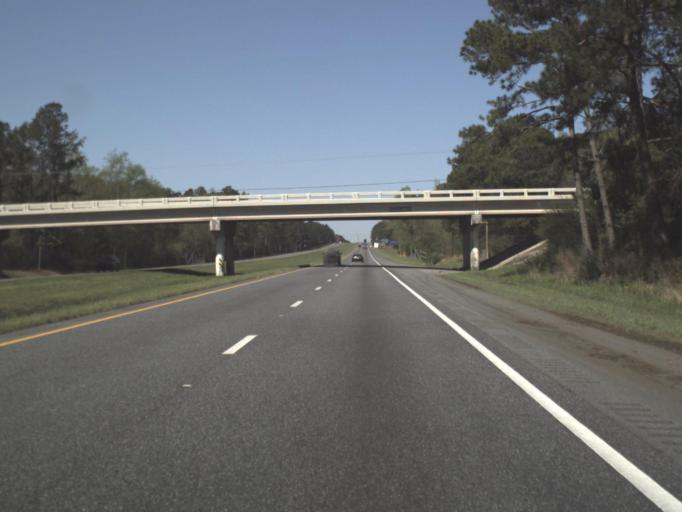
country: US
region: Florida
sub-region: Walton County
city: DeFuniak Springs
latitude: 30.6915
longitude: -86.0942
